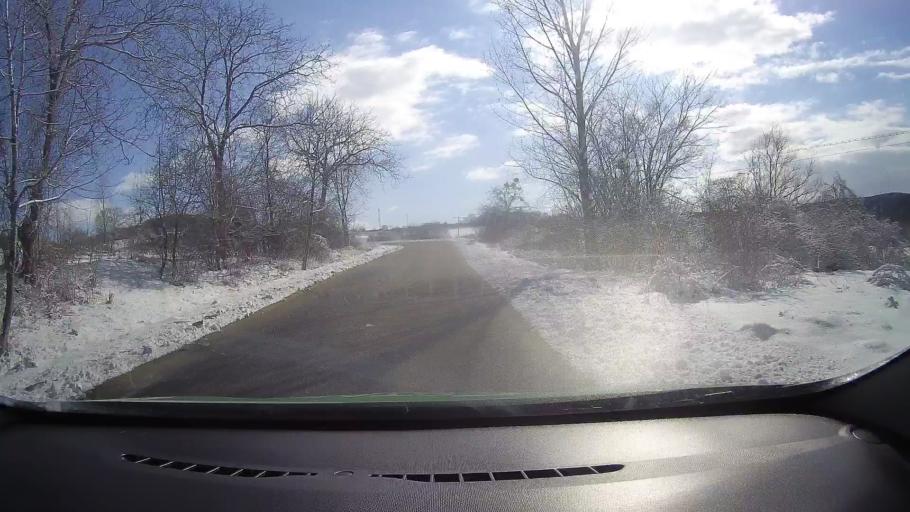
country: RO
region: Sibiu
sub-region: Comuna Mosna
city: Mosna
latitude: 46.0106
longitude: 24.4223
